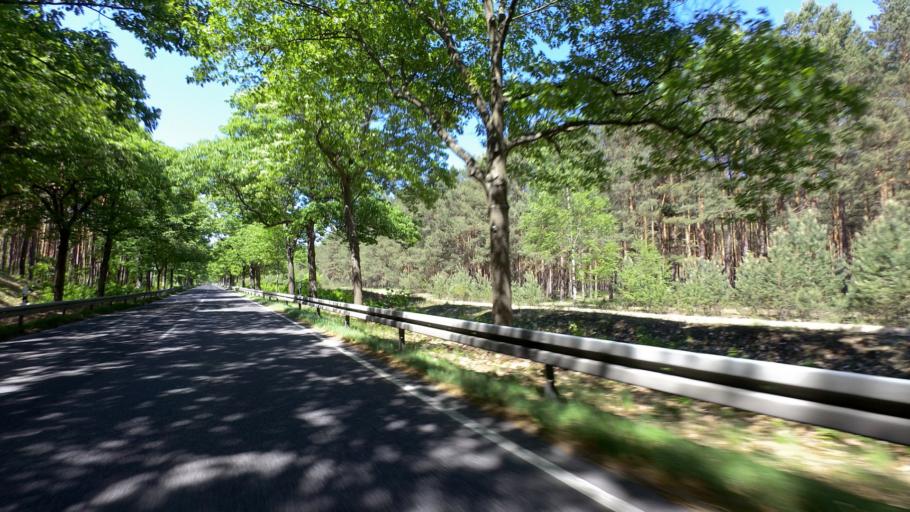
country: DE
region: Brandenburg
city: Drehnow
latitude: 51.8927
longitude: 14.3681
